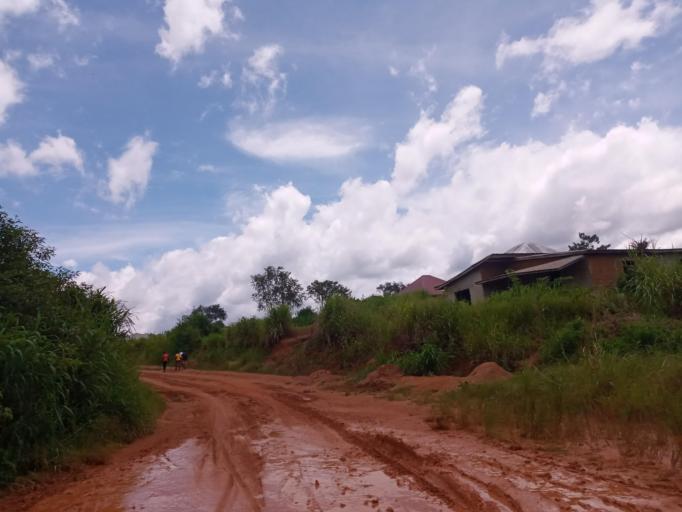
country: SL
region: Eastern Province
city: Koidu
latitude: 8.6447
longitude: -10.9210
